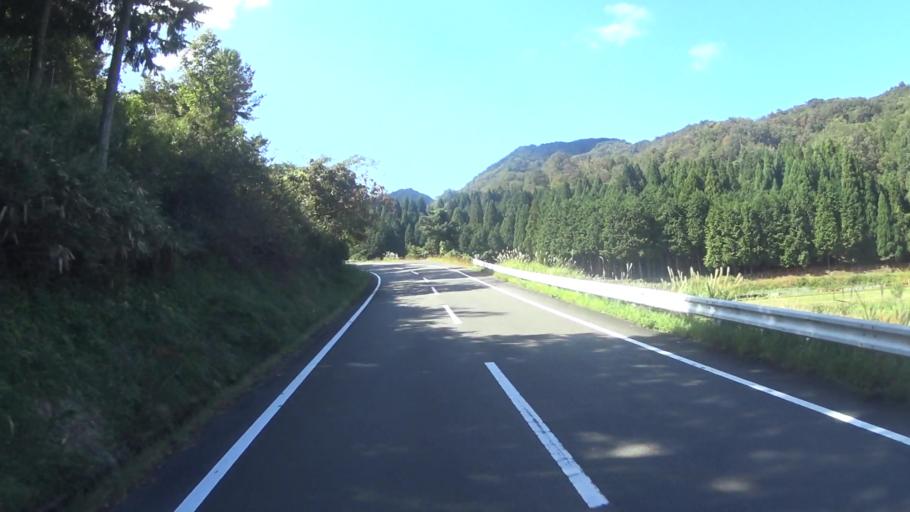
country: JP
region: Hyogo
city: Toyooka
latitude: 35.5350
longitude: 134.9309
